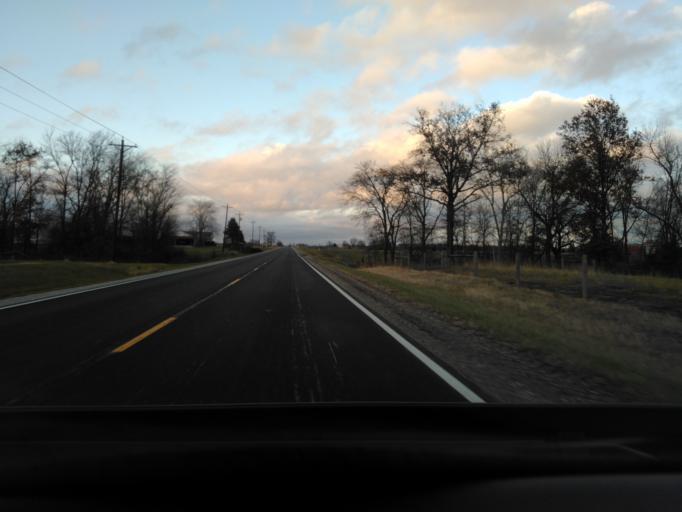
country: US
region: Illinois
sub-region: Effingham County
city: Altamont
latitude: 38.9932
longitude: -88.7487
